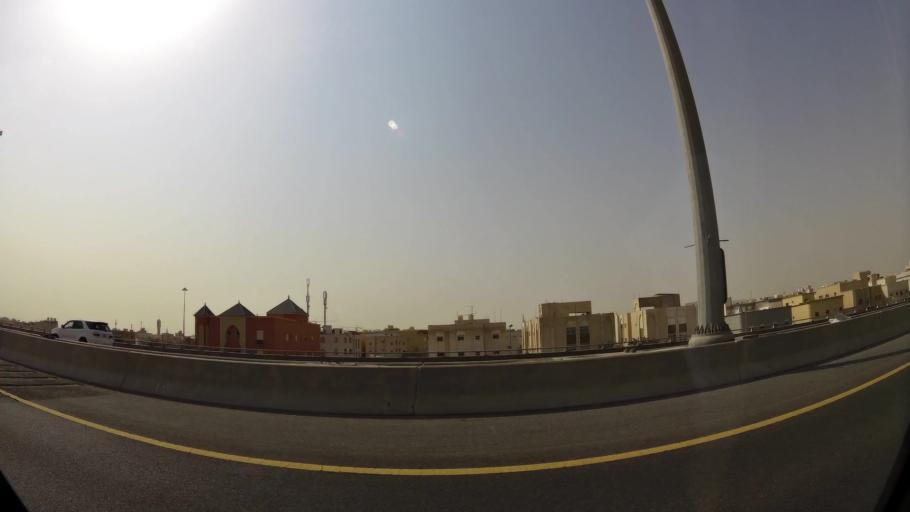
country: KW
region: Muhafazat al Jahra'
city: Al Jahra'
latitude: 29.3534
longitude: 47.6856
